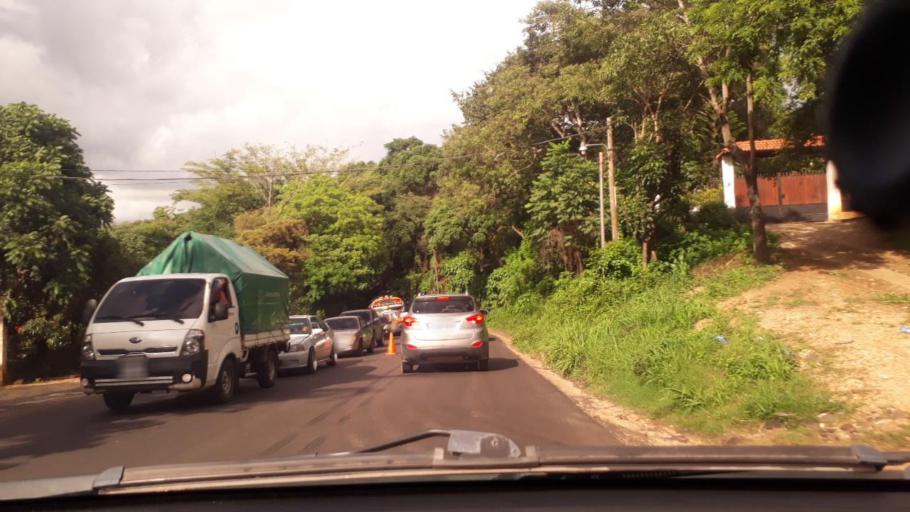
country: GT
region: Jutiapa
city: Quesada
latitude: 14.2711
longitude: -90.0051
